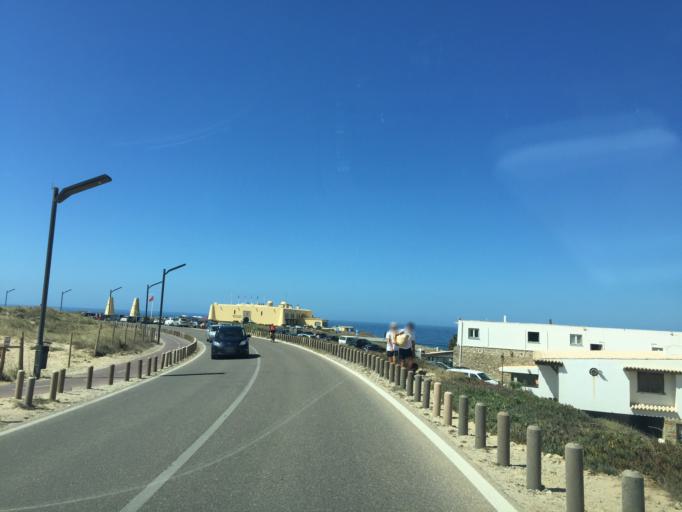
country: PT
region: Lisbon
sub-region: Cascais
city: Cascais
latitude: 38.7296
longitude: -9.4736
